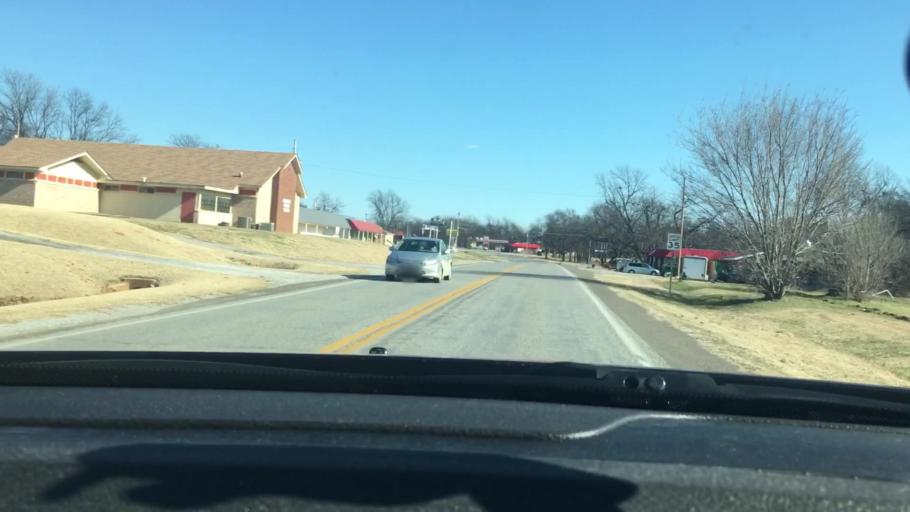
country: US
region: Oklahoma
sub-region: Garvin County
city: Wynnewood
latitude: 34.6441
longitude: -97.1602
